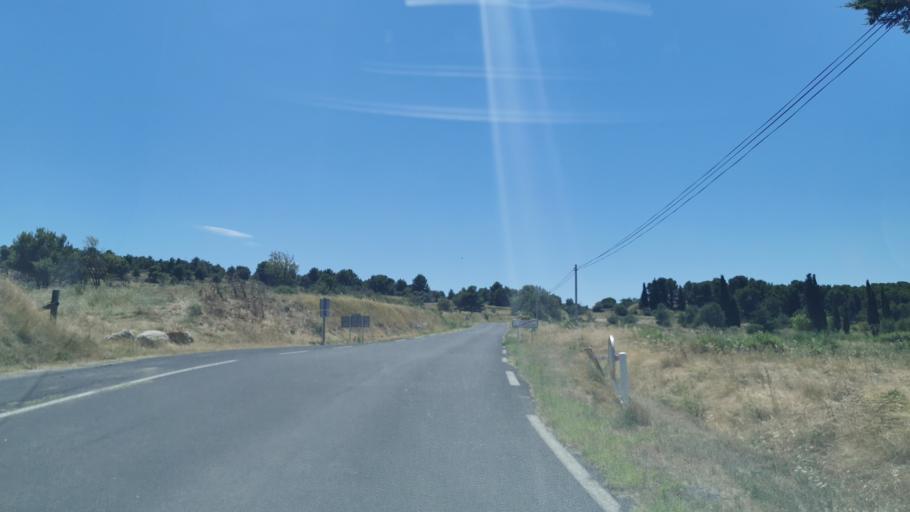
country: FR
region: Languedoc-Roussillon
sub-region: Departement de l'Herault
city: Nissan-lez-Enserune
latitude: 43.2826
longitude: 3.1226
